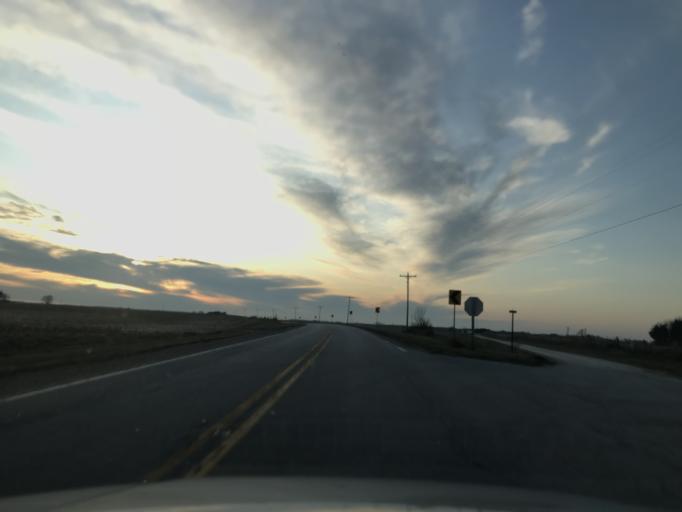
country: US
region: Illinois
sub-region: Warren County
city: Monmouth
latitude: 41.0250
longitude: -90.7763
